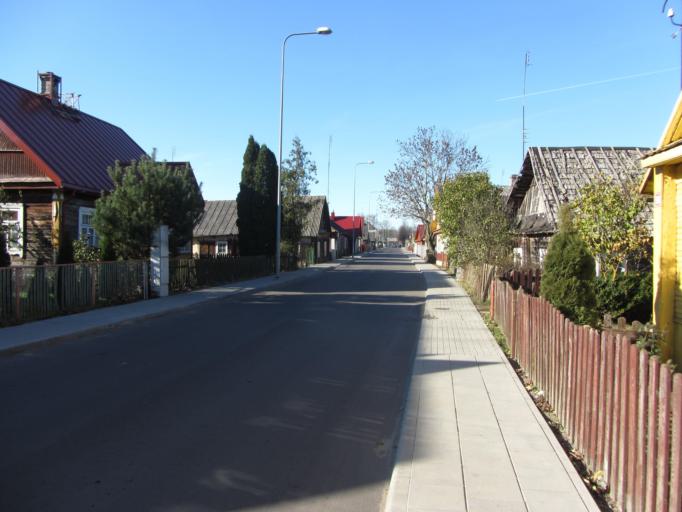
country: LT
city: Eisiskes
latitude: 54.1682
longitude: 25.0002
